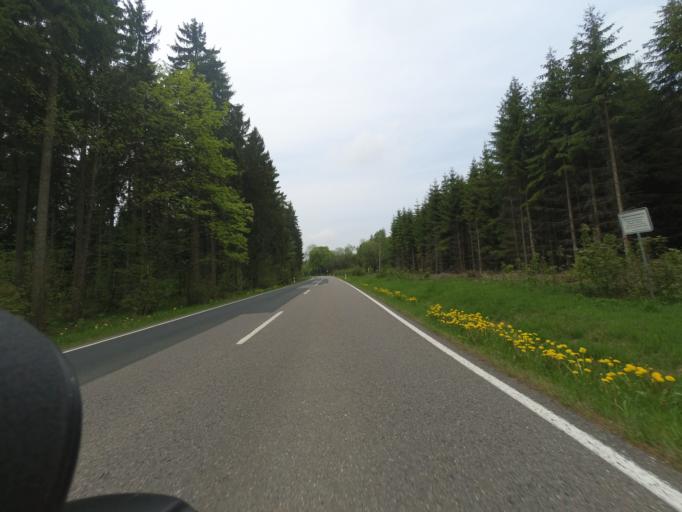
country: DE
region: Saxony
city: Grossruckerswalde
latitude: 50.6524
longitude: 13.1297
